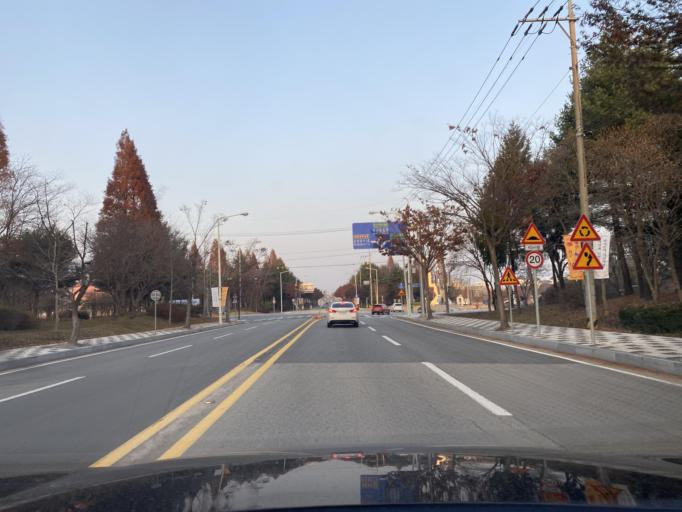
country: KR
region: Chungcheongnam-do
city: Hongsung
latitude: 36.6905
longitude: 126.6574
